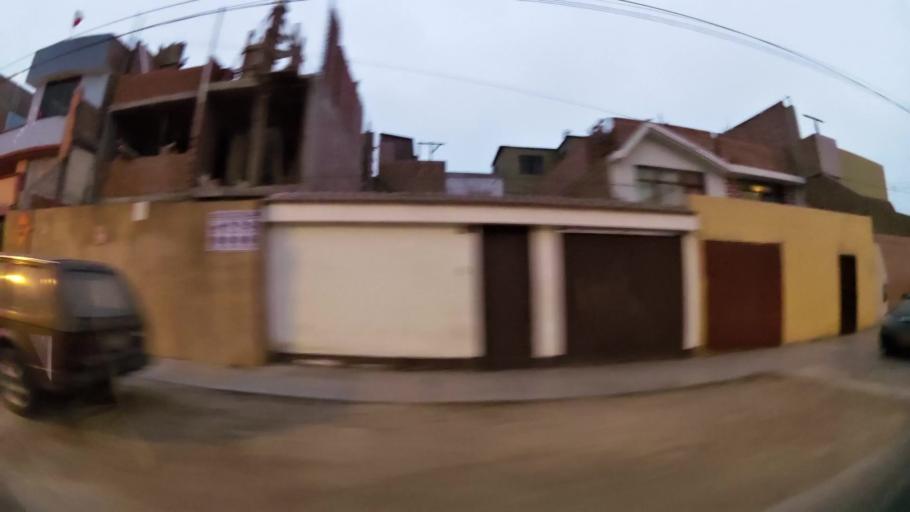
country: PE
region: Callao
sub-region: Callao
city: Callao
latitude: -12.0814
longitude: -77.0994
